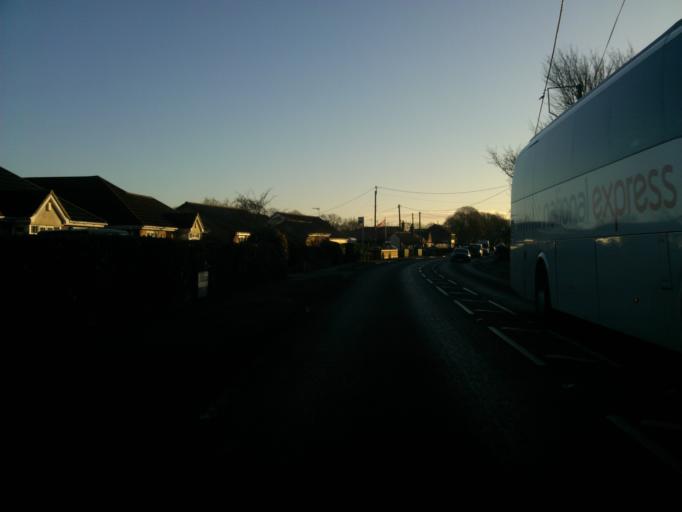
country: GB
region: England
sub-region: Essex
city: Great Bentley
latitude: 51.8409
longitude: 1.0364
